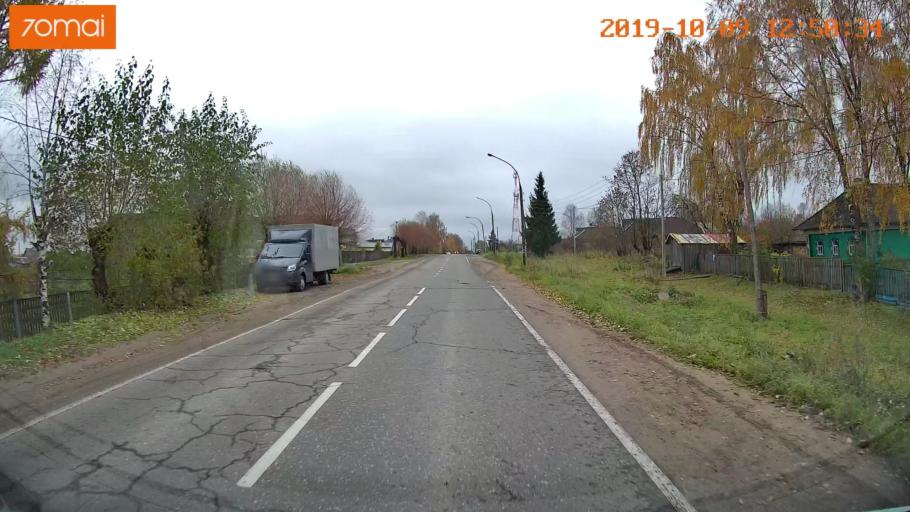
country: RU
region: Jaroslavl
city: Prechistoye
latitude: 58.4225
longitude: 40.3328
